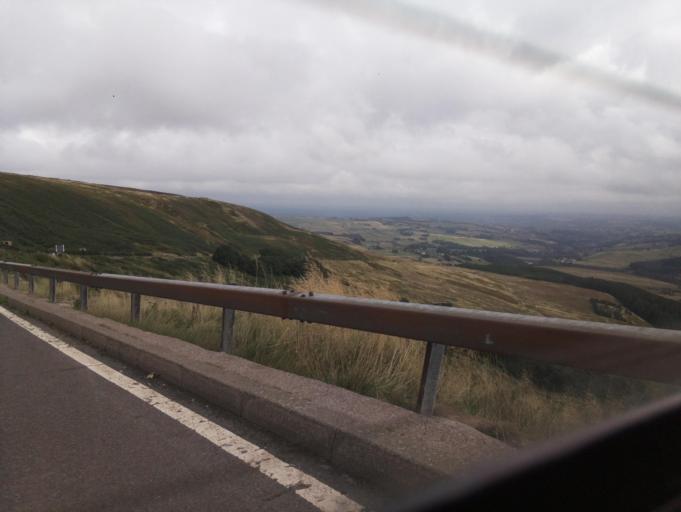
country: GB
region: England
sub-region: Kirklees
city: Meltham
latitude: 53.5330
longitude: -1.8544
